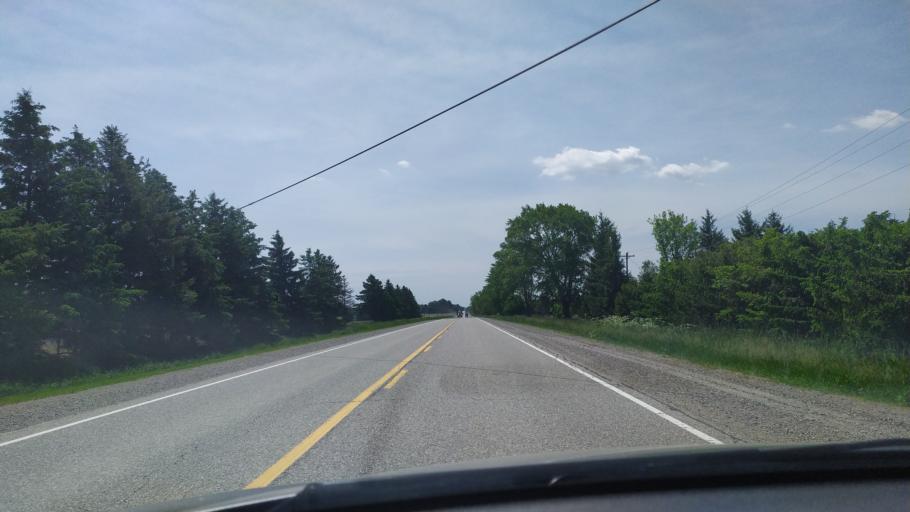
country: CA
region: Ontario
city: Dorchester
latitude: 43.1189
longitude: -81.0199
